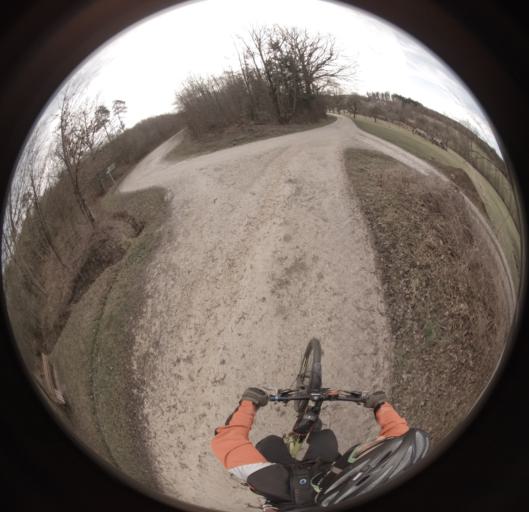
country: DE
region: Baden-Wuerttemberg
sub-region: Regierungsbezirk Stuttgart
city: Ottenbach
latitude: 48.7262
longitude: 9.7324
